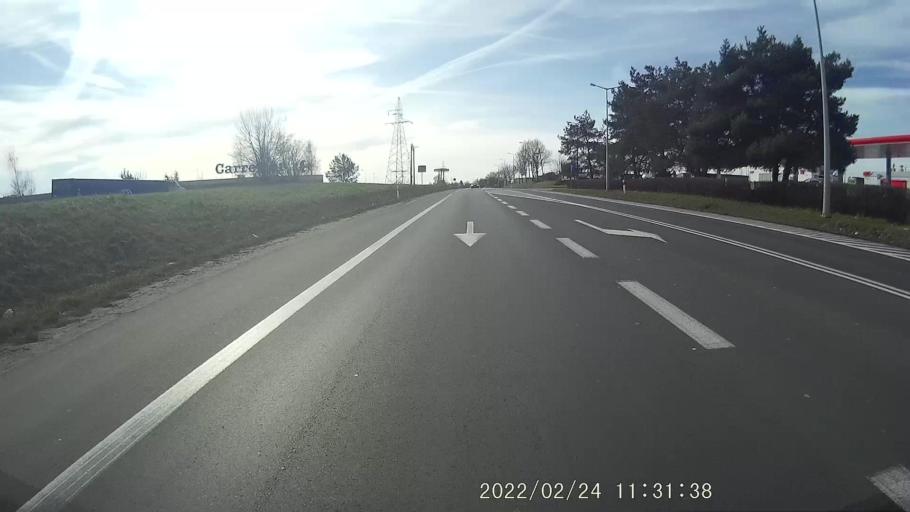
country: PL
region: Lower Silesian Voivodeship
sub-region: Powiat polkowicki
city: Przemkow
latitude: 51.5226
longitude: 15.7355
